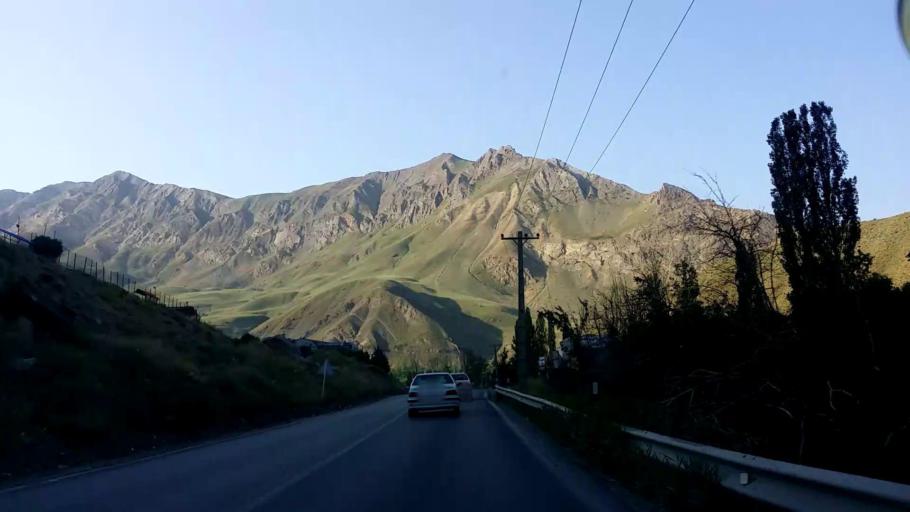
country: IR
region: Tehran
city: Tajrish
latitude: 36.0838
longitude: 51.3165
